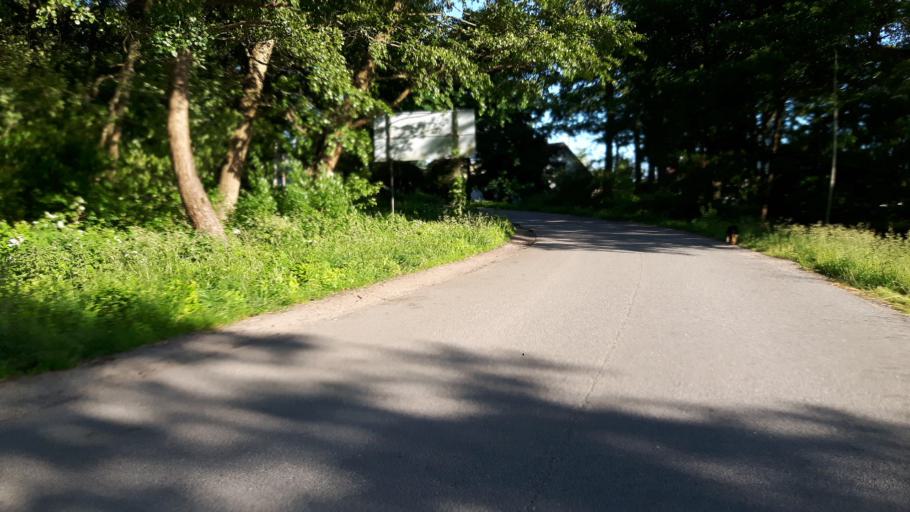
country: LT
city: Nida
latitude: 55.1571
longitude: 20.8452
